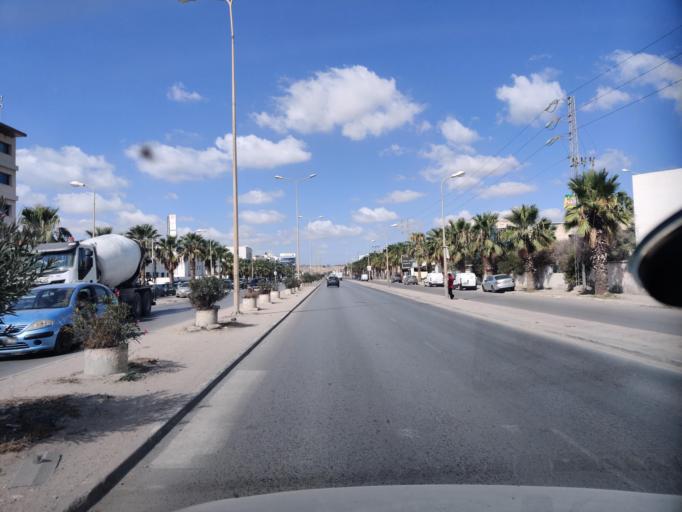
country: TN
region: Bin 'Arus
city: Ben Arous
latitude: 36.7742
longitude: 10.2191
